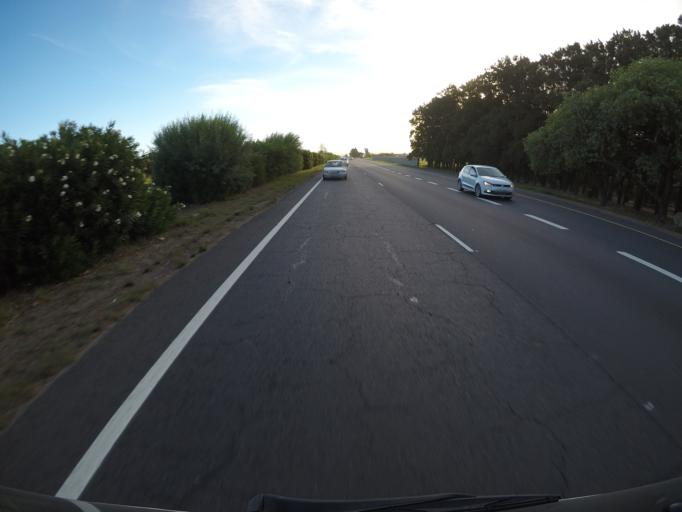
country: ZA
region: Western Cape
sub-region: City of Cape Town
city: Kraaifontein
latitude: -33.8262
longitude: 18.7687
